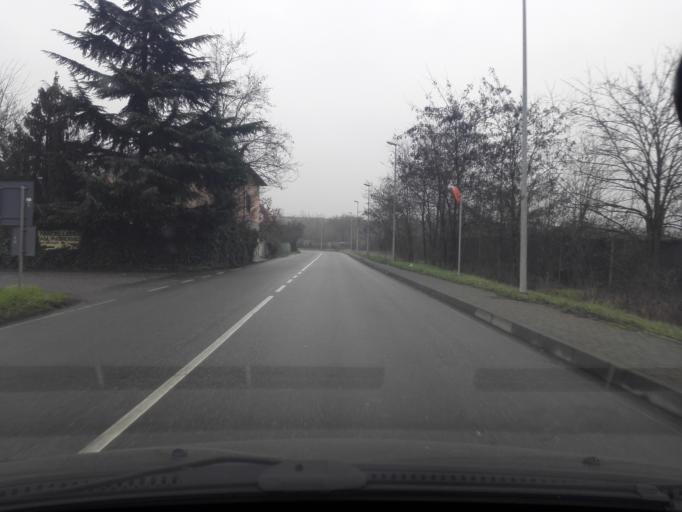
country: IT
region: Piedmont
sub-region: Provincia di Alessandria
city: Novi Ligure
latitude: 44.7701
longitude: 8.7745
